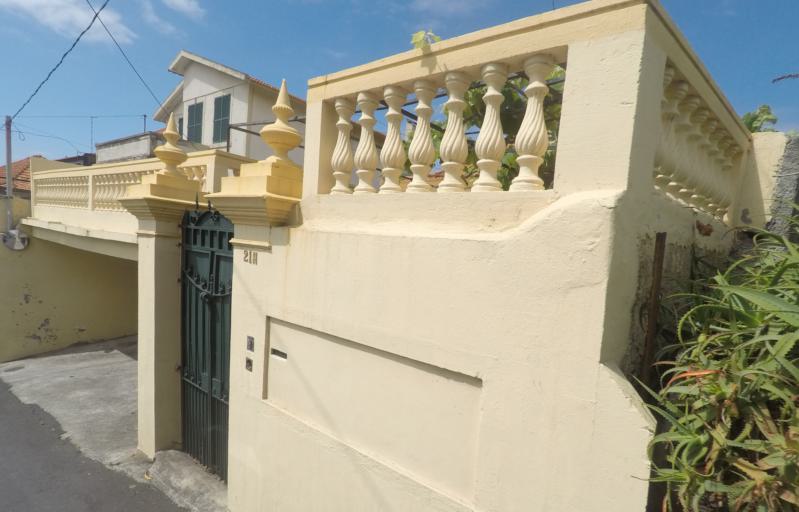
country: PT
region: Madeira
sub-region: Funchal
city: Nossa Senhora do Monte
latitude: 32.6502
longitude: -16.9229
